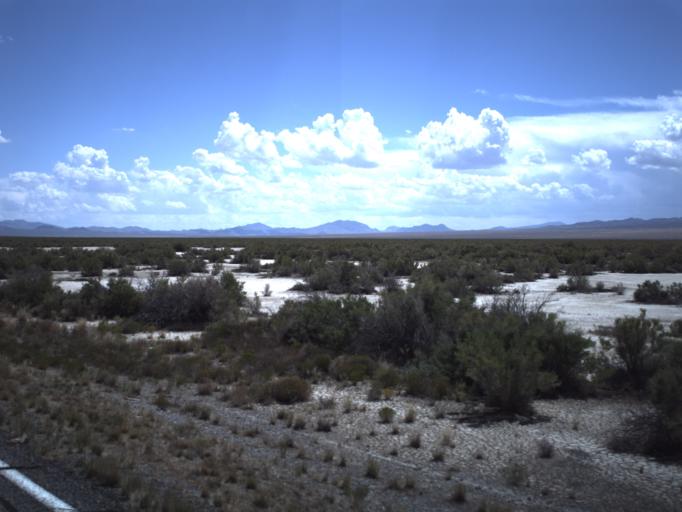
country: US
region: Nevada
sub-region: White Pine County
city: McGill
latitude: 39.0466
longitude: -113.9115
